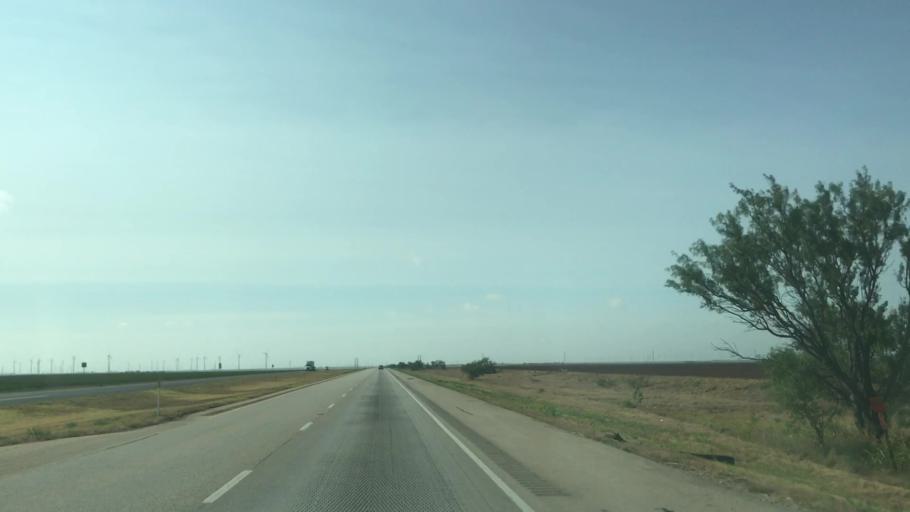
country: US
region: Texas
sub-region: Scurry County
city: Snyder
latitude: 32.6143
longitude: -100.7496
